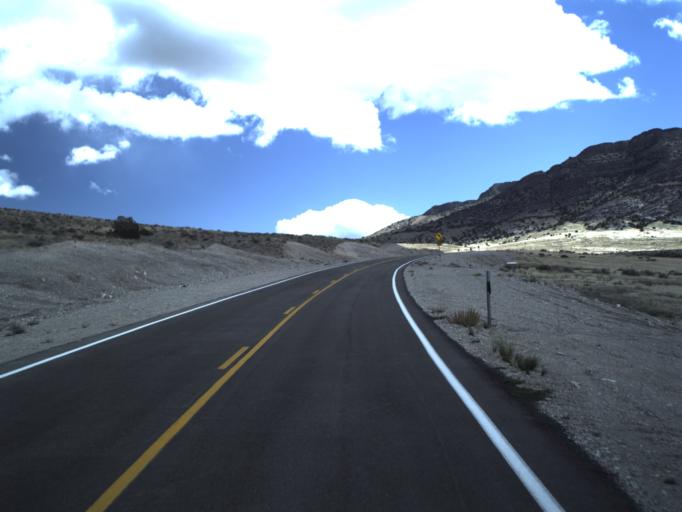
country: US
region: Utah
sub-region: Beaver County
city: Milford
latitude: 38.5059
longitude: -113.6008
